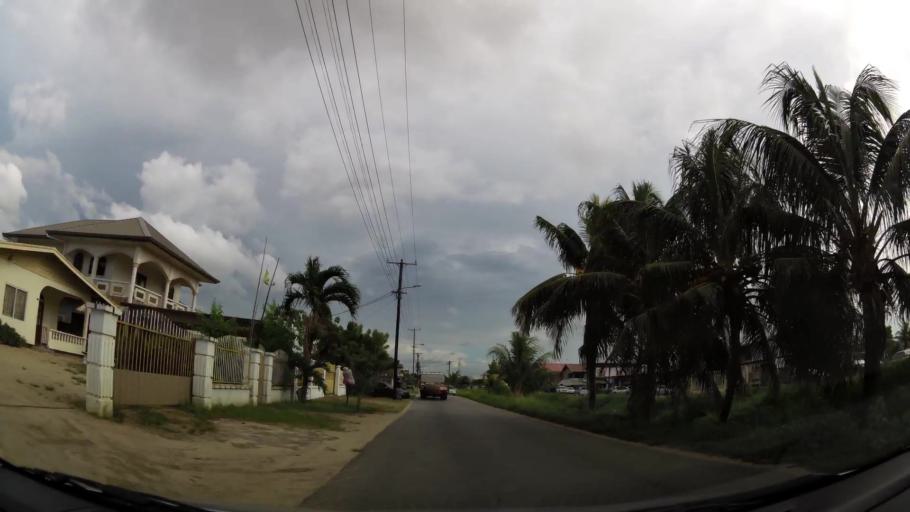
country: SR
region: Paramaribo
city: Paramaribo
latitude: 5.8516
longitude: -55.1835
